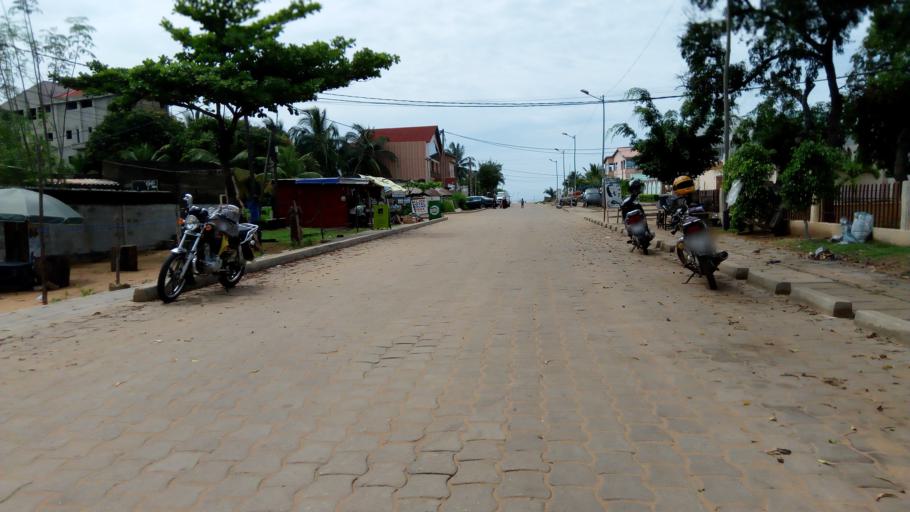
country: TG
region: Maritime
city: Lome
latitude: 6.1634
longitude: 1.3265
